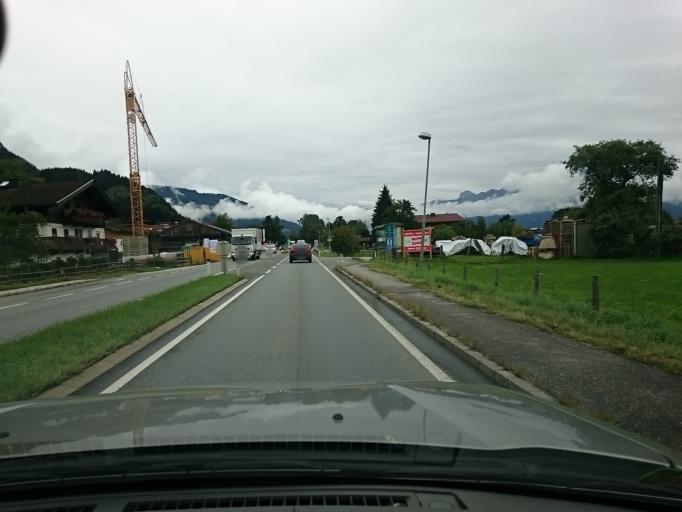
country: AT
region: Salzburg
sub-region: Politischer Bezirk Zell am See
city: Maishofen
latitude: 47.3558
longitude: 12.7998
